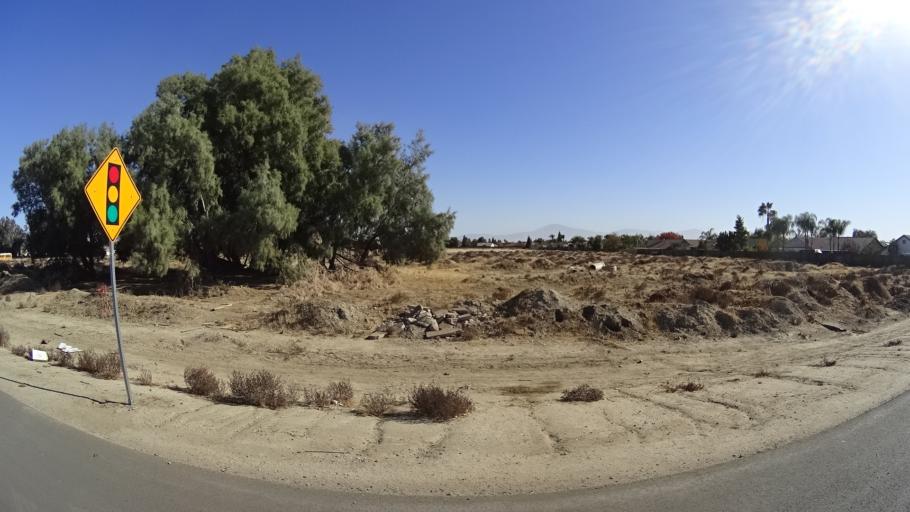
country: US
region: California
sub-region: Kern County
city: Greenfield
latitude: 35.2875
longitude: -119.0566
